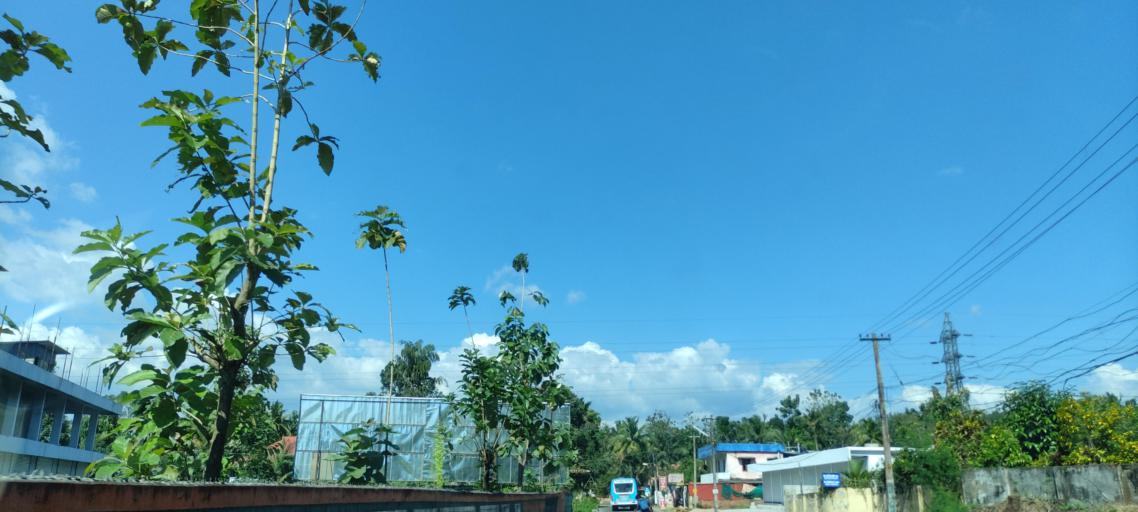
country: IN
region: Kerala
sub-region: Pattanamtitta
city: Adur
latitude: 9.1592
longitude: 76.7430
